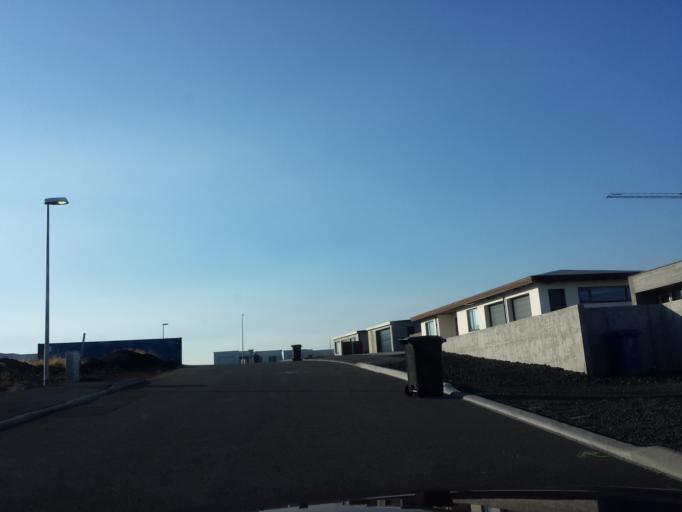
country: IS
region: Capital Region
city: Reykjavik
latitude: 64.0855
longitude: -21.8429
